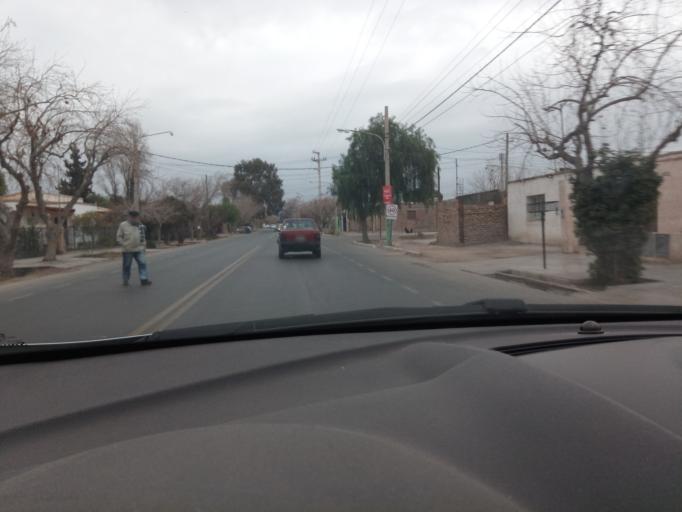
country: AR
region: San Juan
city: San Juan
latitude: -31.5508
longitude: -68.5665
